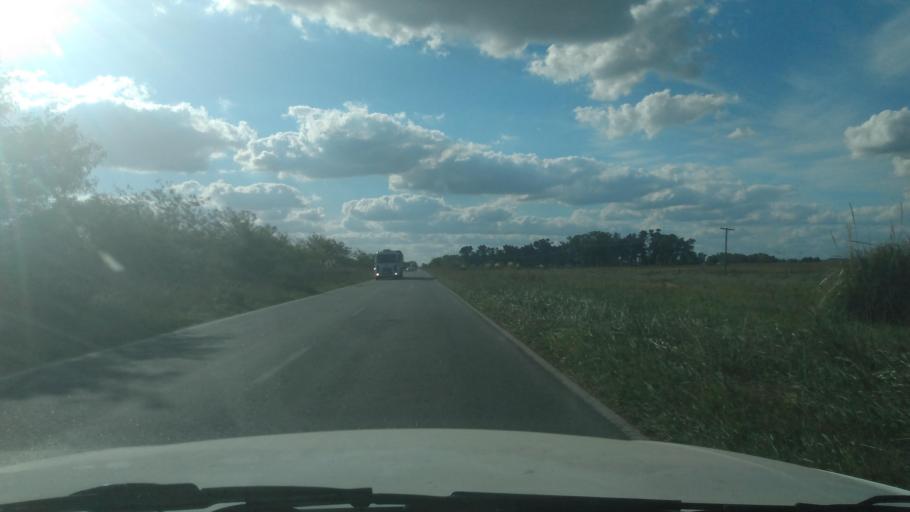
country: AR
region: Buenos Aires
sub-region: Partido de Mercedes
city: Mercedes
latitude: -34.7654
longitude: -59.3737
